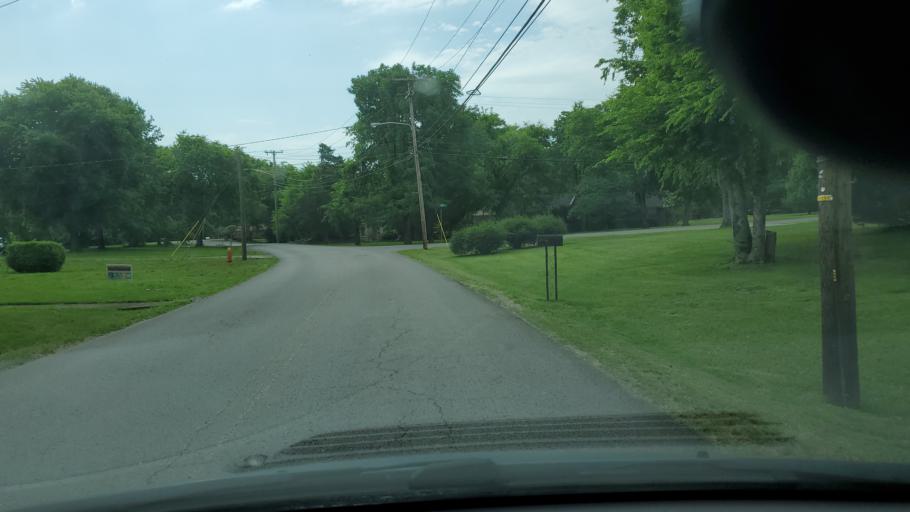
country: US
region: Tennessee
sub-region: Davidson County
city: Lakewood
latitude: 36.2298
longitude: -86.7179
